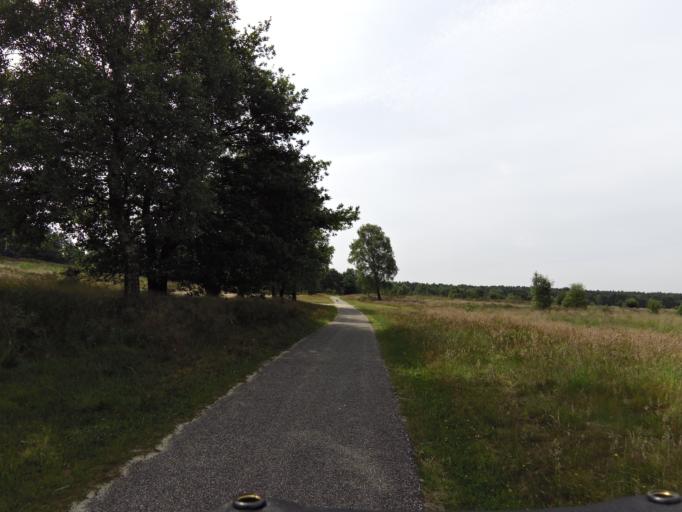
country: NL
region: Gelderland
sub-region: Gemeente Rozendaal
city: Rozendaal
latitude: 52.0274
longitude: 5.9807
